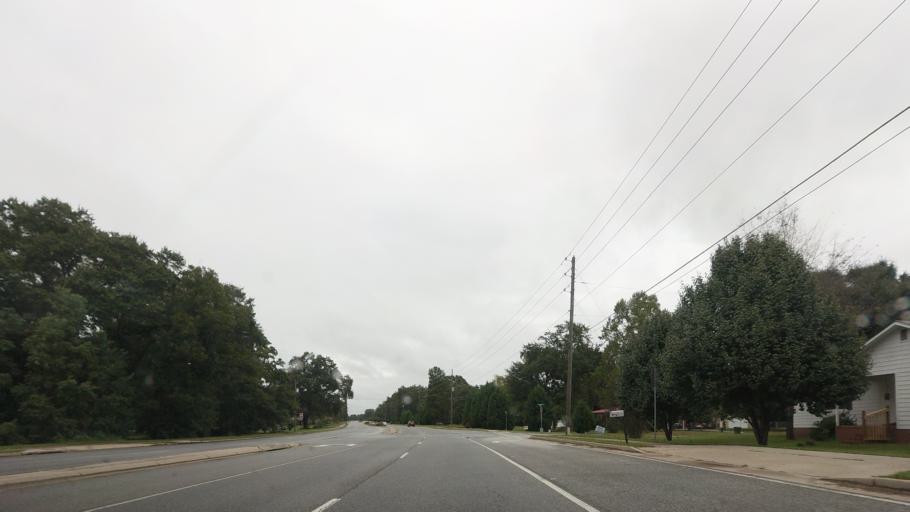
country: US
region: Georgia
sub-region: Houston County
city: Centerville
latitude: 32.5379
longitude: -83.6598
